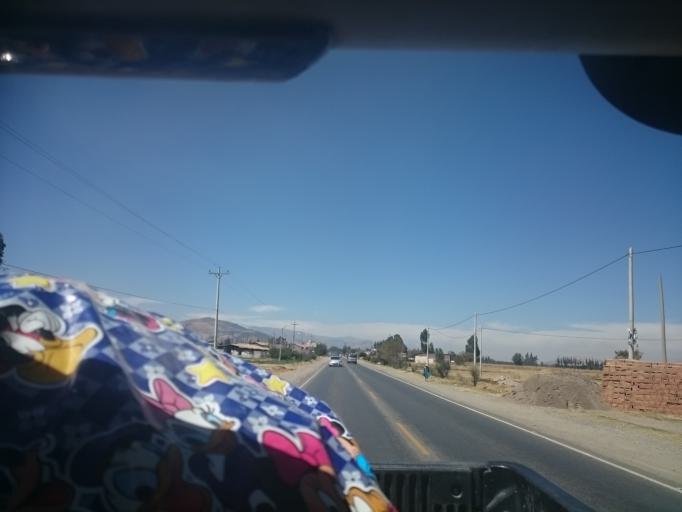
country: PE
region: Junin
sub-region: Provincia de Jauja
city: San Lorenzo
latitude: -11.8300
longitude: -75.4021
